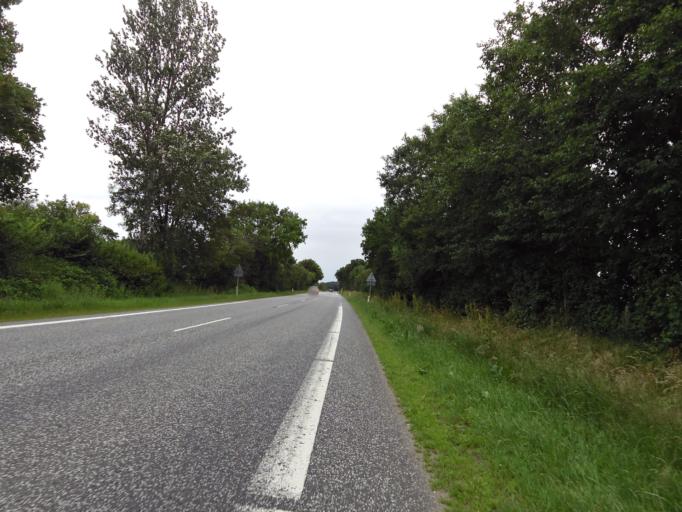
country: DK
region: South Denmark
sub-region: Tonder Kommune
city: Logumkloster
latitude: 55.1011
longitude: 8.9419
